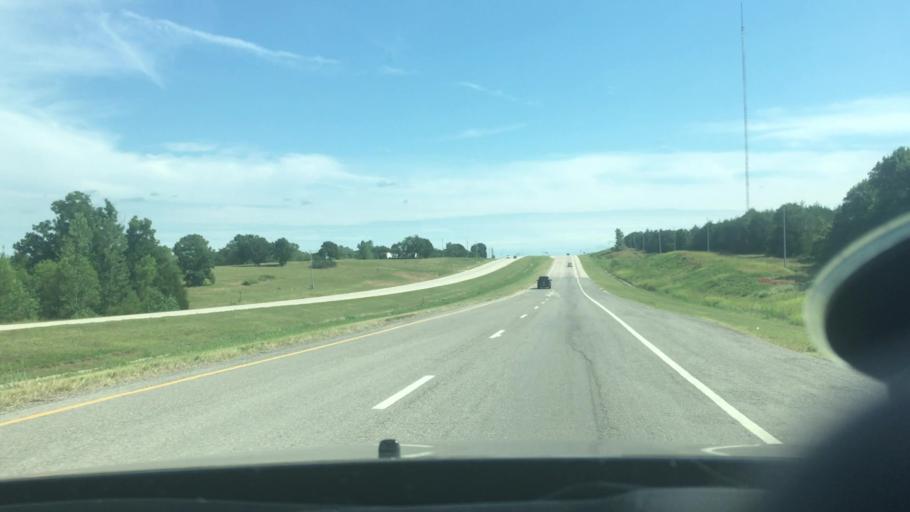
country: US
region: Oklahoma
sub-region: Pontotoc County
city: Byng
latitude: 34.9099
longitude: -96.6787
